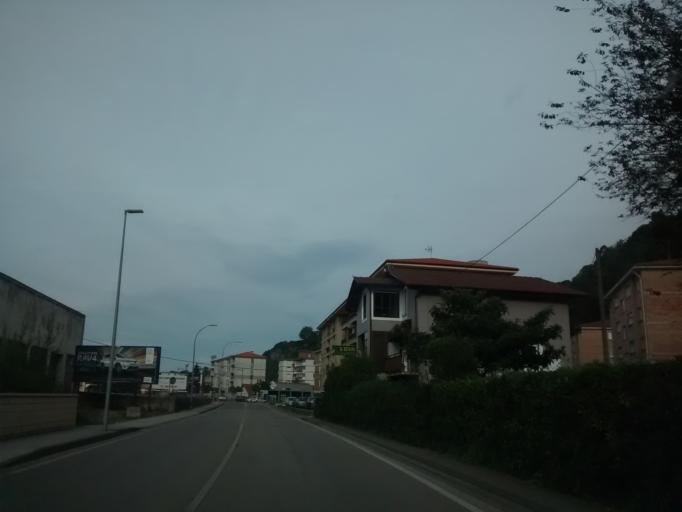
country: ES
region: Cantabria
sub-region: Provincia de Cantabria
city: Laredo
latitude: 43.4049
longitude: -3.4184
